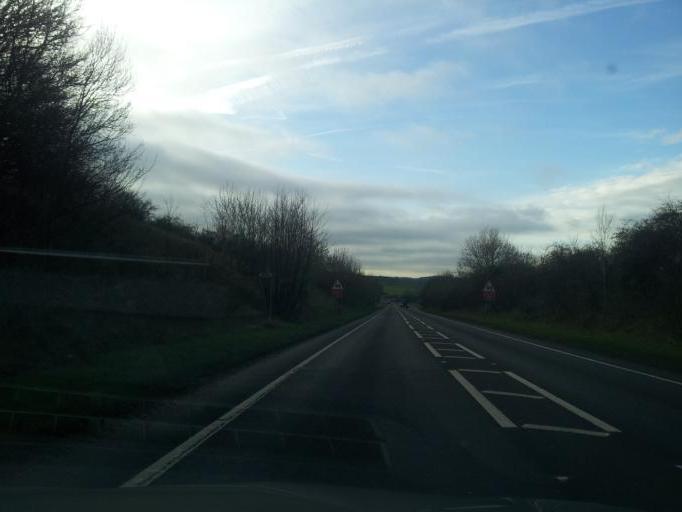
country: GB
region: England
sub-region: District of Rutland
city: Ketton
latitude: 52.5951
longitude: -0.5392
